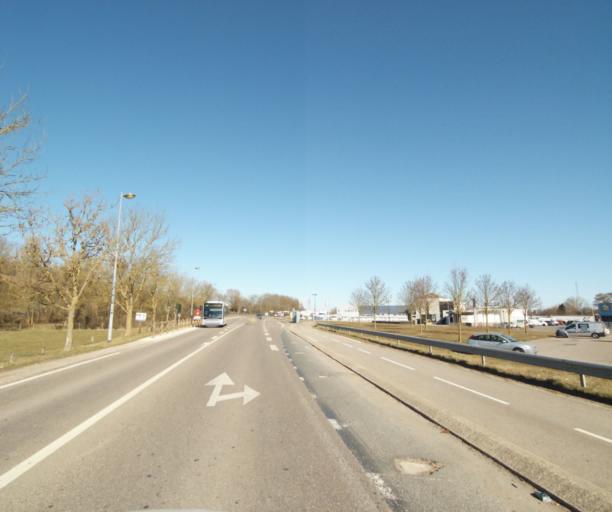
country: FR
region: Lorraine
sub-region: Departement de Meurthe-et-Moselle
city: Ludres
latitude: 48.6240
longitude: 6.1784
